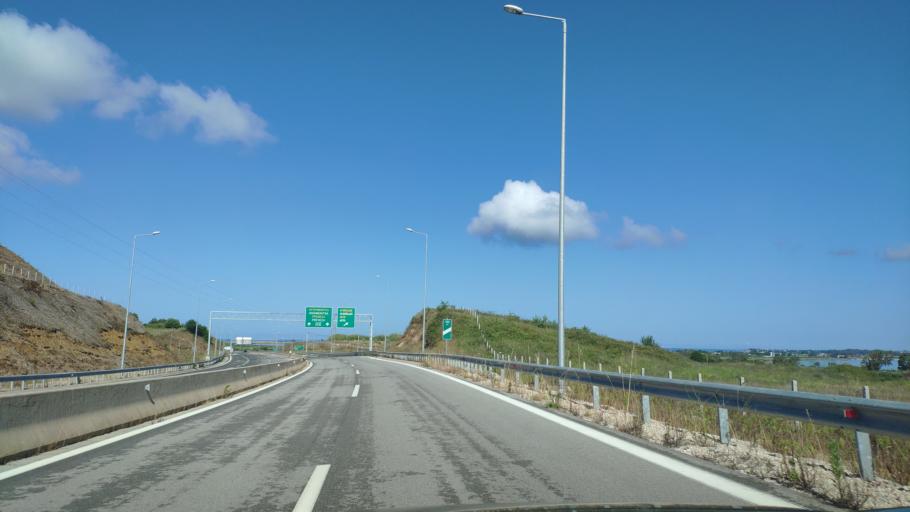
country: GR
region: Epirus
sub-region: Nomos Prevezis
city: Preveza
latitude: 38.9133
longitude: 20.8083
